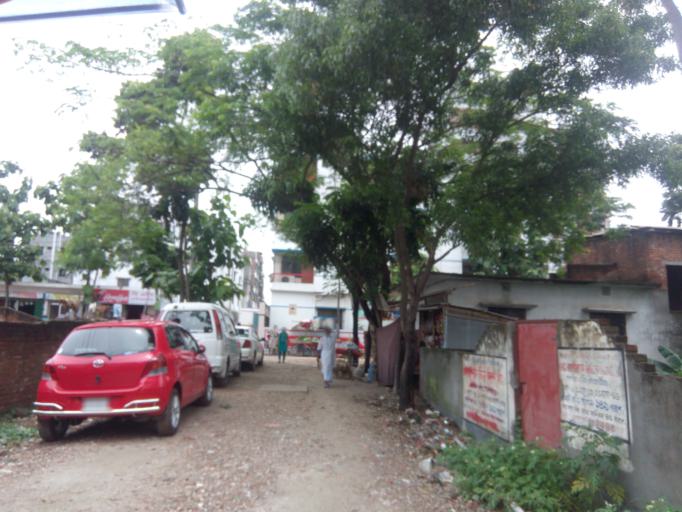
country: BD
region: Dhaka
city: Azimpur
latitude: 23.7449
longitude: 90.3522
